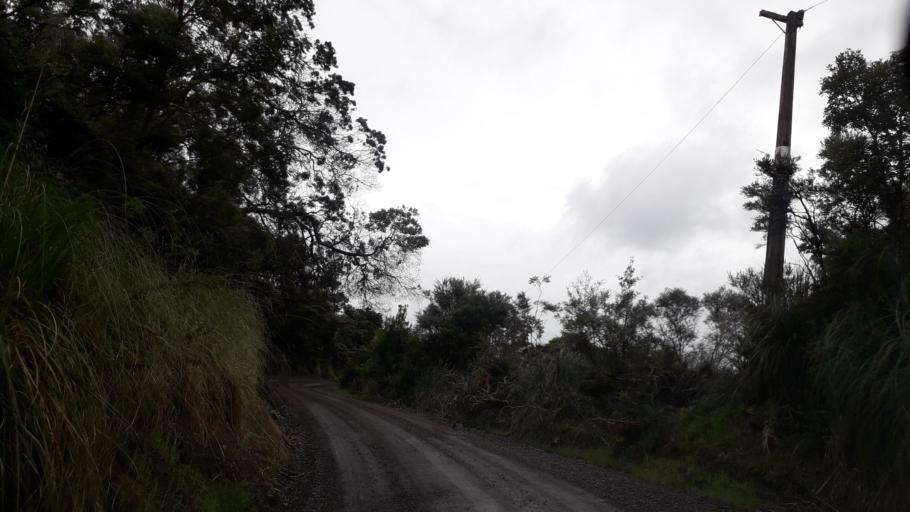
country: NZ
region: Northland
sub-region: Far North District
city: Kaitaia
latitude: -35.3817
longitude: 173.4100
